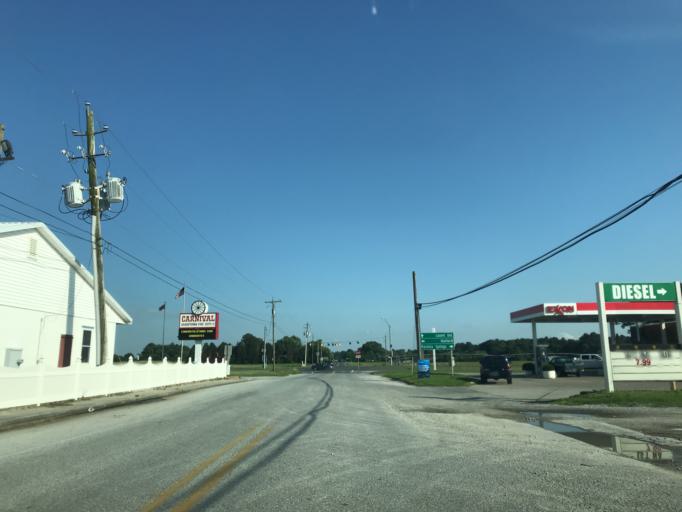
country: US
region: Maryland
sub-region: Wicomico County
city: Hebron
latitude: 38.5343
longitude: -75.7160
